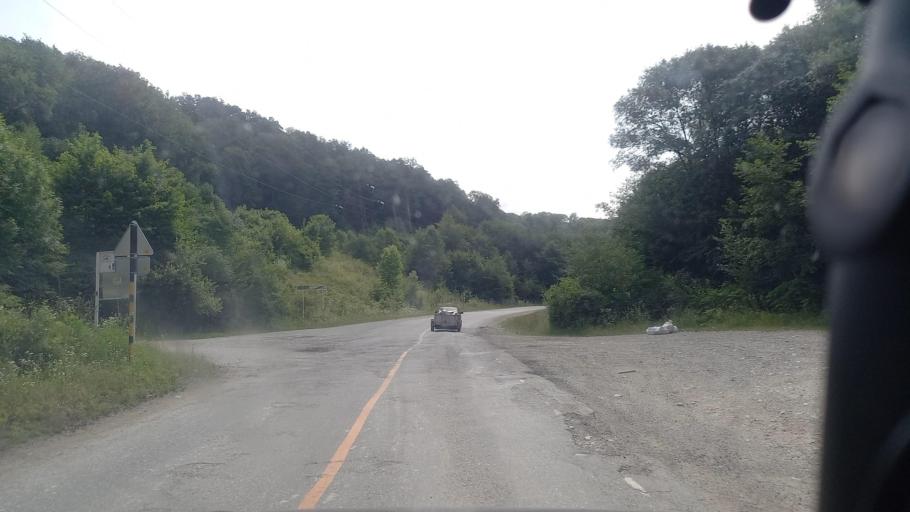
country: RU
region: Karachayevo-Cherkesiya
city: Kurdzhinovo
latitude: 44.0150
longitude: 40.9542
